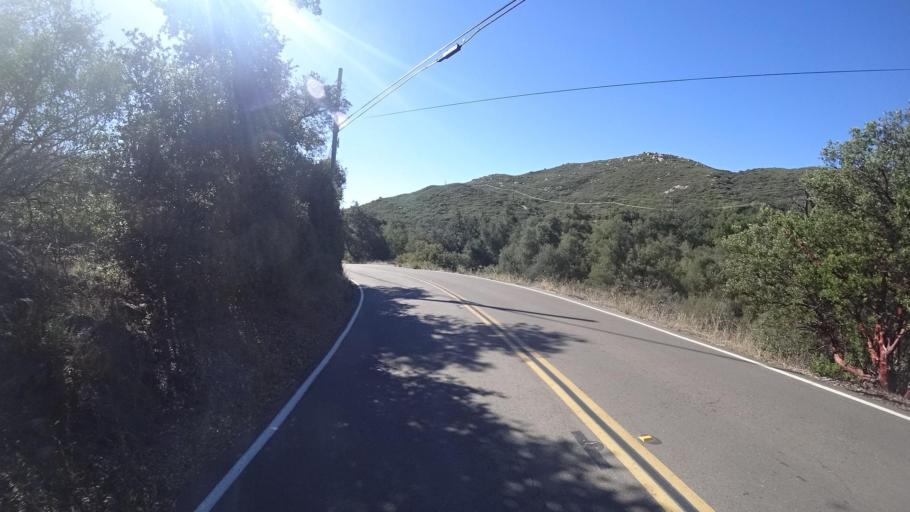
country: US
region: California
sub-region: San Diego County
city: Descanso
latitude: 32.8574
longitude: -116.6307
